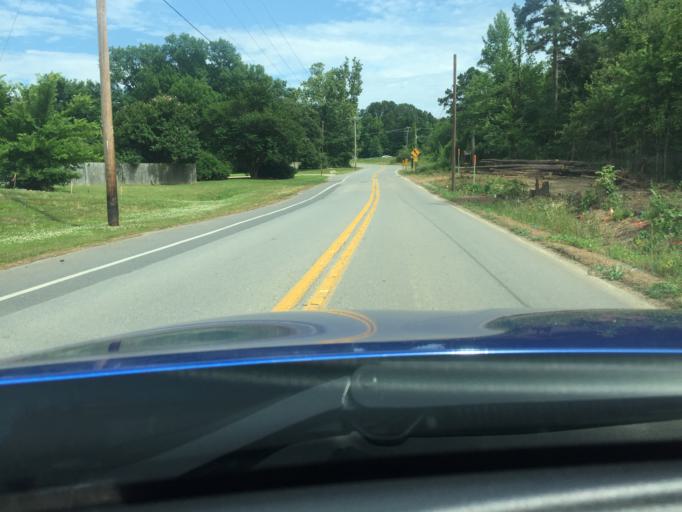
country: US
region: Arkansas
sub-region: Pulaski County
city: Maumelle
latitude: 34.8043
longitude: -92.4349
